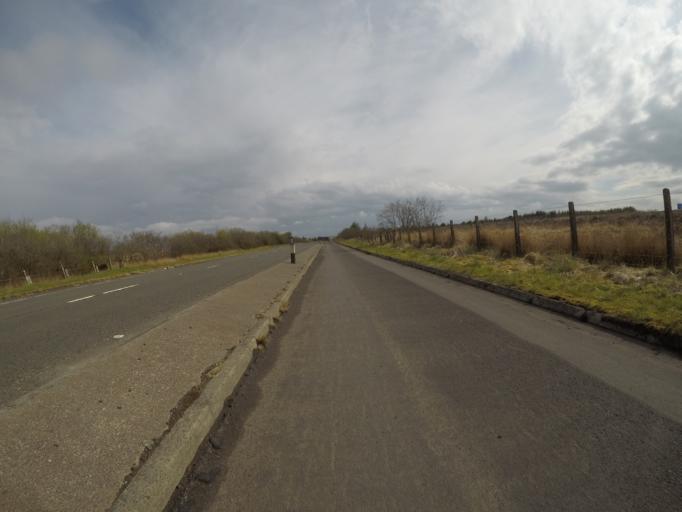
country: GB
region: Scotland
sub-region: East Renfrewshire
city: Neilston
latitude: 55.7016
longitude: -4.3958
